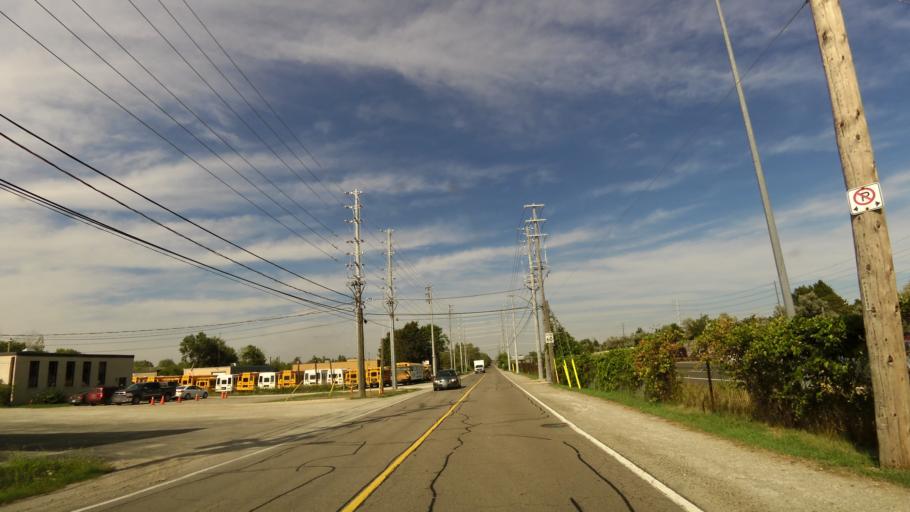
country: CA
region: Ontario
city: Mississauga
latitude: 43.5291
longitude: -79.6431
